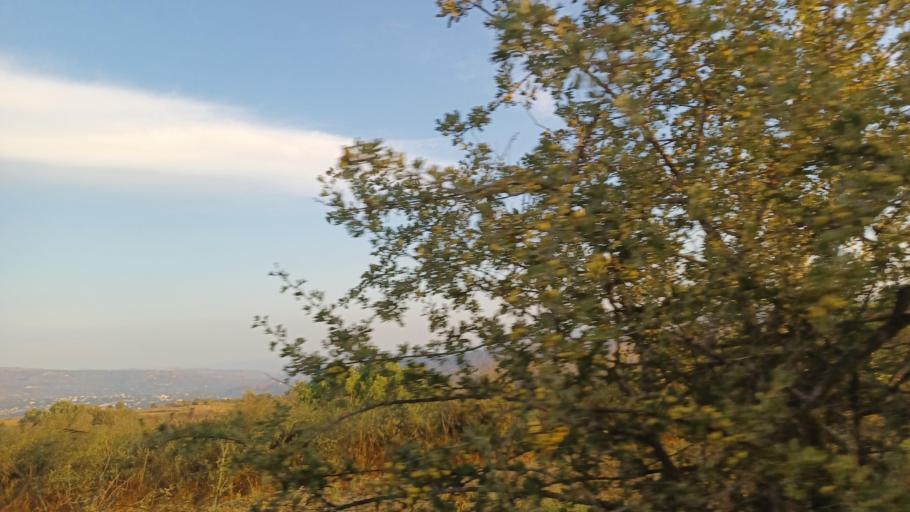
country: CY
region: Pafos
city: Tala
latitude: 34.8980
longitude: 32.4998
